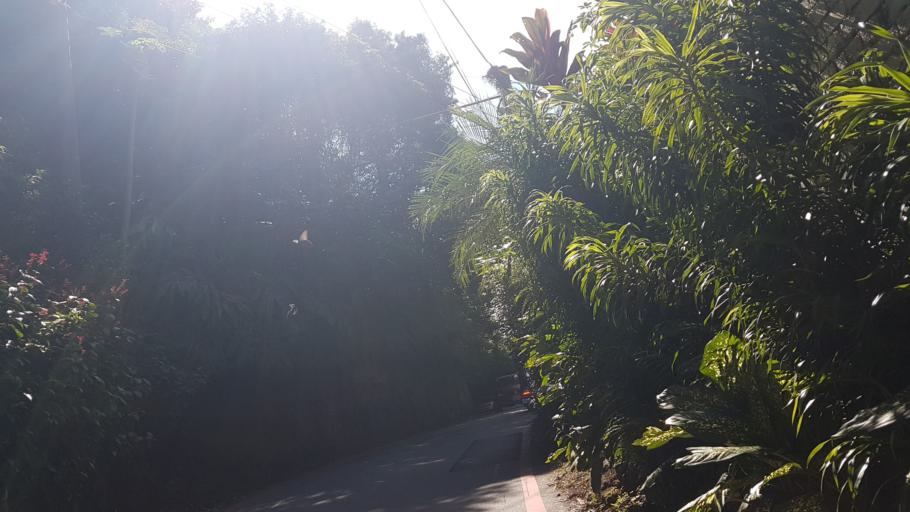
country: TW
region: Taipei
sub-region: Taipei
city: Banqiao
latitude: 24.9525
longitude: 121.5317
